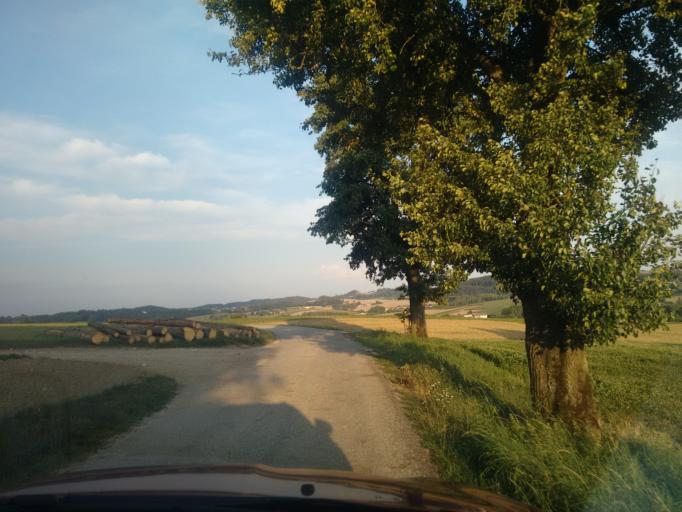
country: AT
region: Upper Austria
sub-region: Politischer Bezirk Grieskirchen
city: Bad Schallerbach
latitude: 48.2001
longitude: 13.9076
